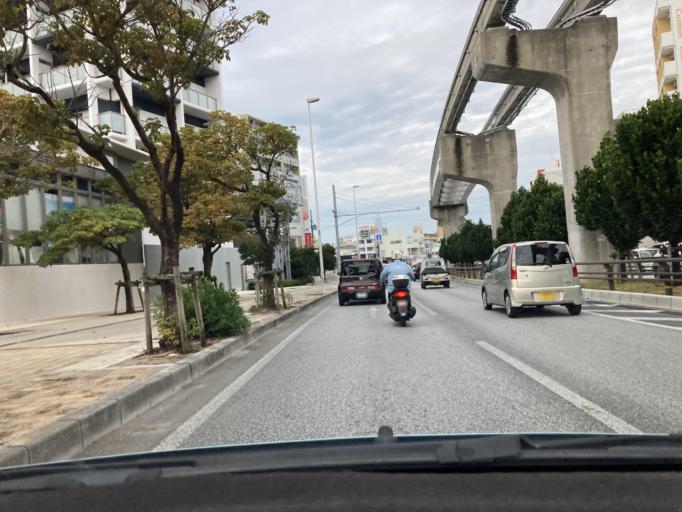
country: JP
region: Okinawa
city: Naha-shi
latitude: 26.2240
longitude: 127.6985
